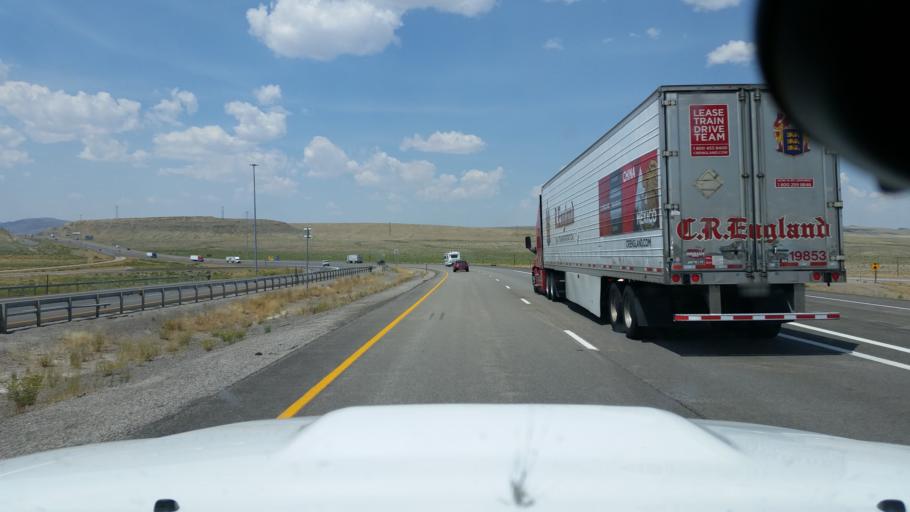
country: US
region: Wyoming
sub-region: Carbon County
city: Rawlins
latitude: 41.7794
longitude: -107.1249
